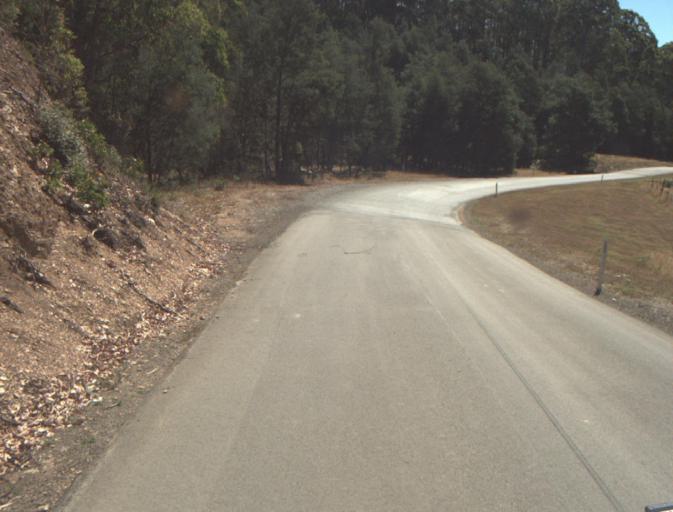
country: AU
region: Tasmania
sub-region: Dorset
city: Scottsdale
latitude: -41.3118
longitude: 147.3998
